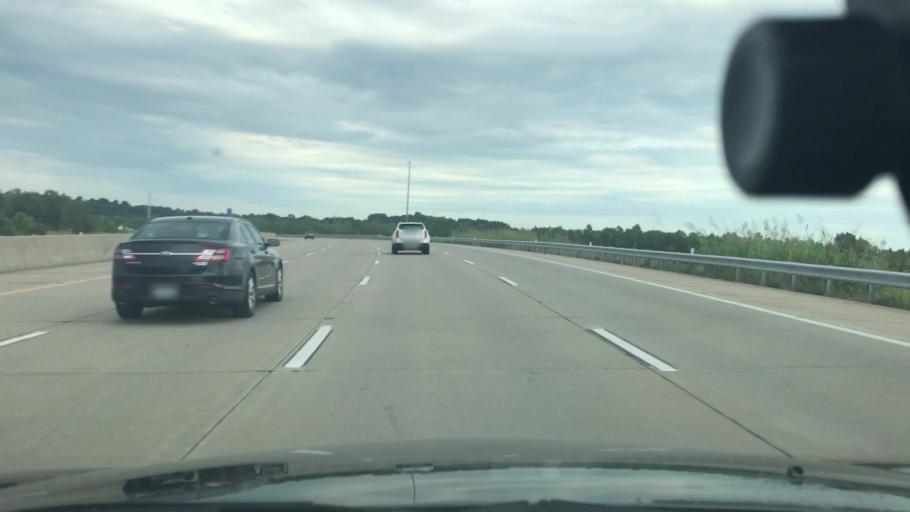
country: US
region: Missouri
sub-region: Saint Louis County
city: Maryland Heights
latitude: 38.7091
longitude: -90.5048
